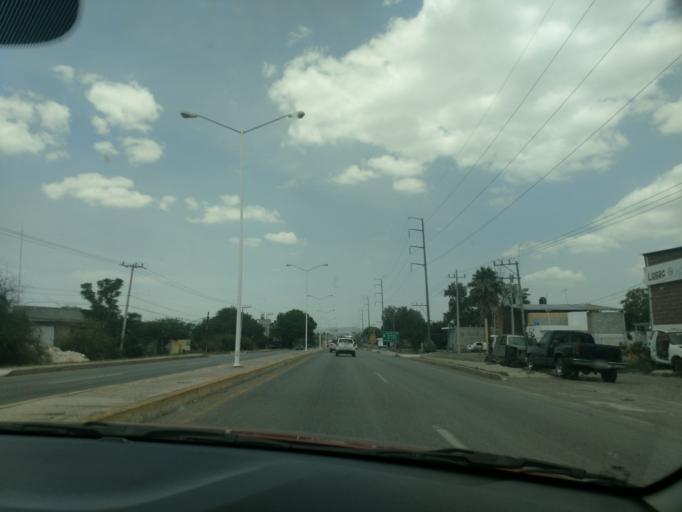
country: MX
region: San Luis Potosi
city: Rio Verde
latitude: 21.9220
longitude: -99.9707
